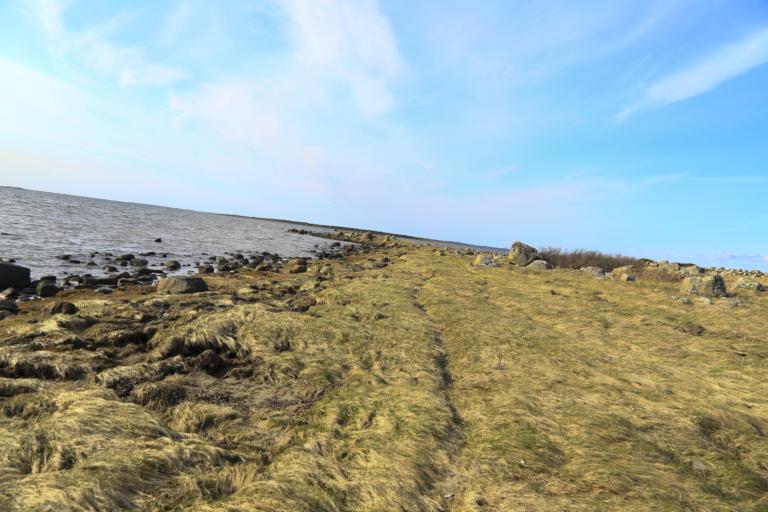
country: SE
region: Halland
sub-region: Varbergs Kommun
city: Varberg
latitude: 57.1288
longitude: 12.2122
